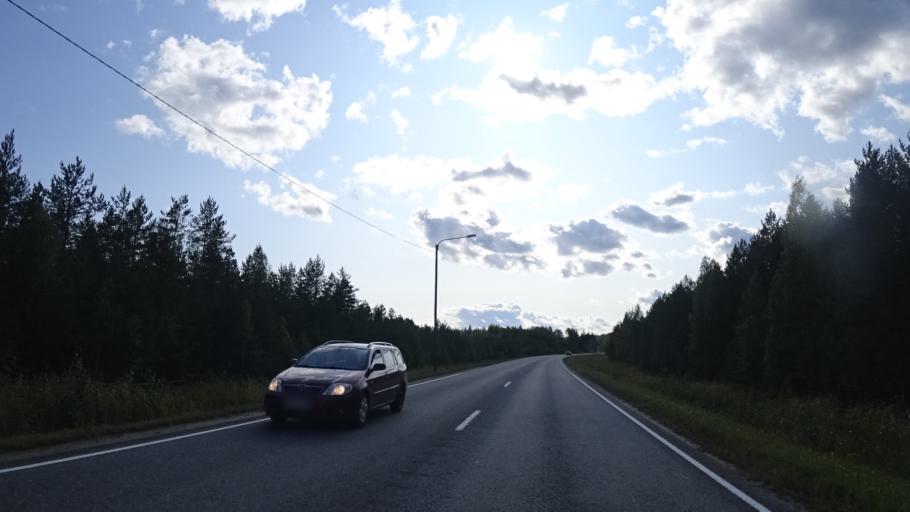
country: FI
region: North Karelia
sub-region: Keski-Karjala
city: Kitee
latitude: 62.0968
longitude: 30.1070
